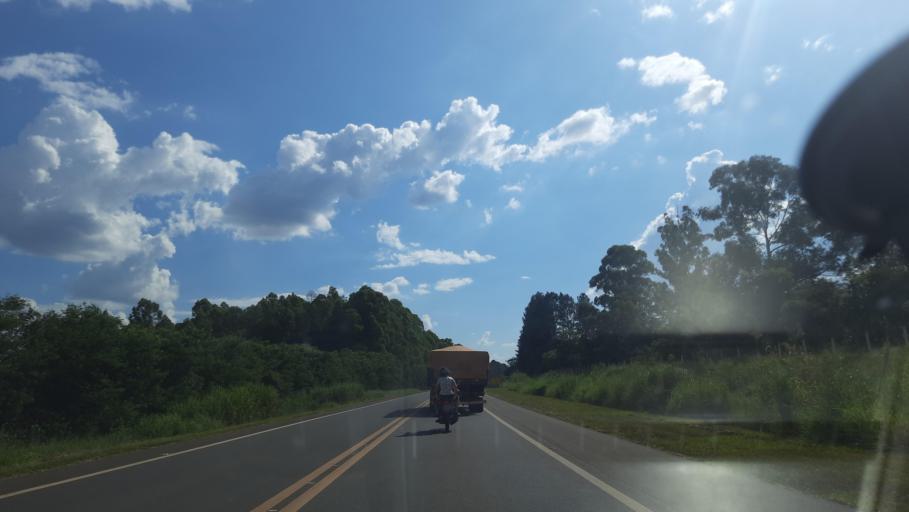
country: BR
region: Sao Paulo
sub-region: Casa Branca
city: Casa Branca
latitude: -21.7560
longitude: -47.0031
